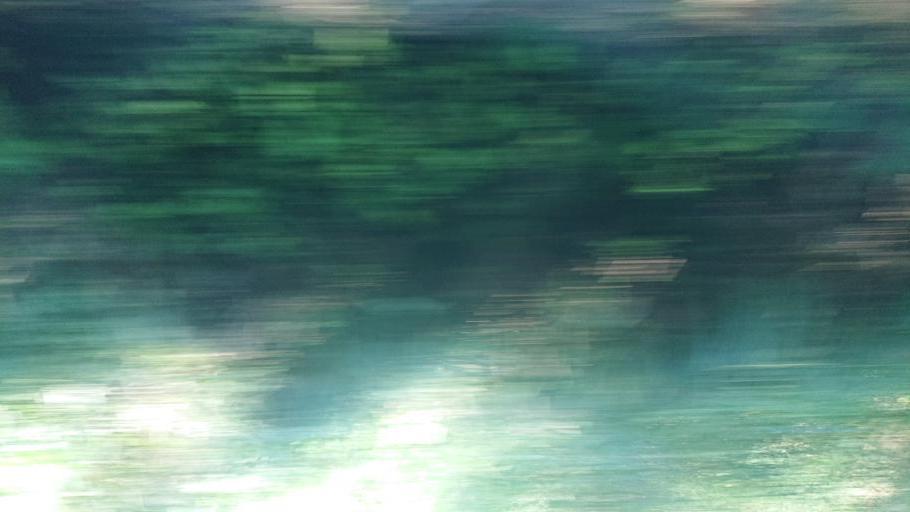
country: TW
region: Taiwan
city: Lugu
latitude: 23.4970
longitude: 120.7888
